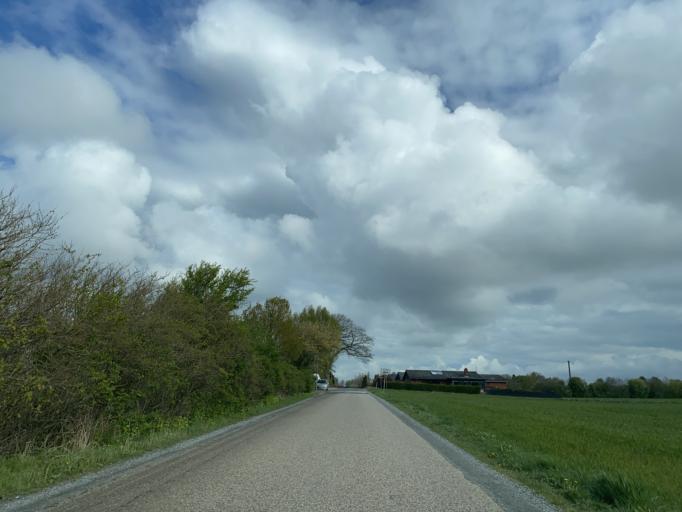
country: DK
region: Central Jutland
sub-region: Silkeborg Kommune
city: Silkeborg
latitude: 56.2128
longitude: 9.5179
